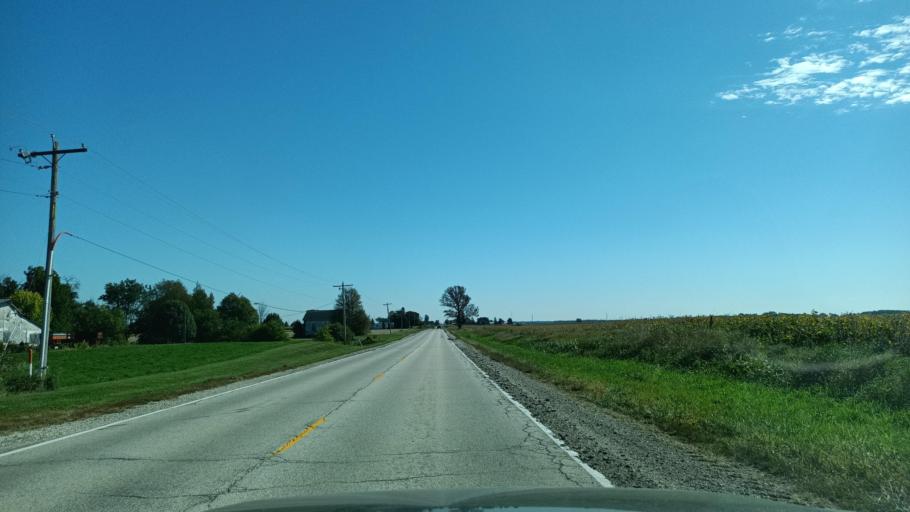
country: US
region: Illinois
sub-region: Knox County
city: Knoxville
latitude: 40.9080
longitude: -90.2341
